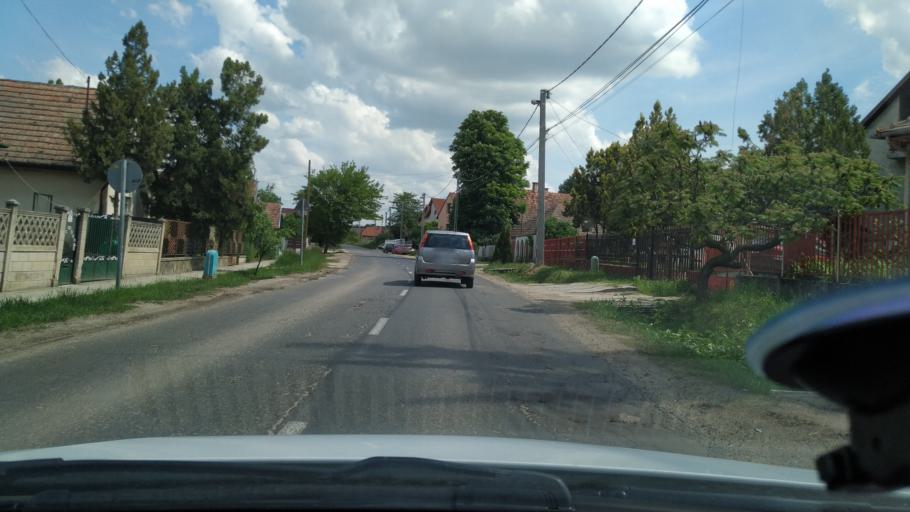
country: HU
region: Pest
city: Gyomro
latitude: 47.4111
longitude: 19.3997
